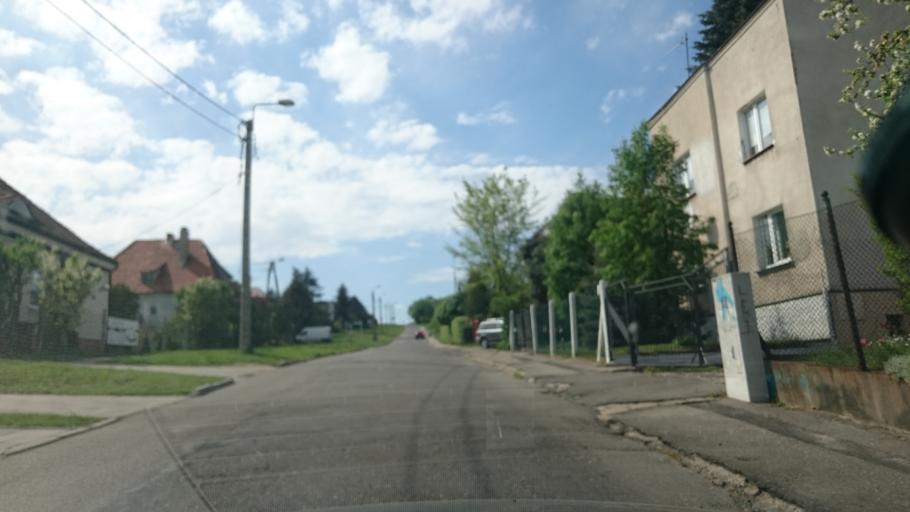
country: PL
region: Kujawsko-Pomorskie
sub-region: Grudziadz
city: Grudziadz
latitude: 53.4645
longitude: 18.7379
